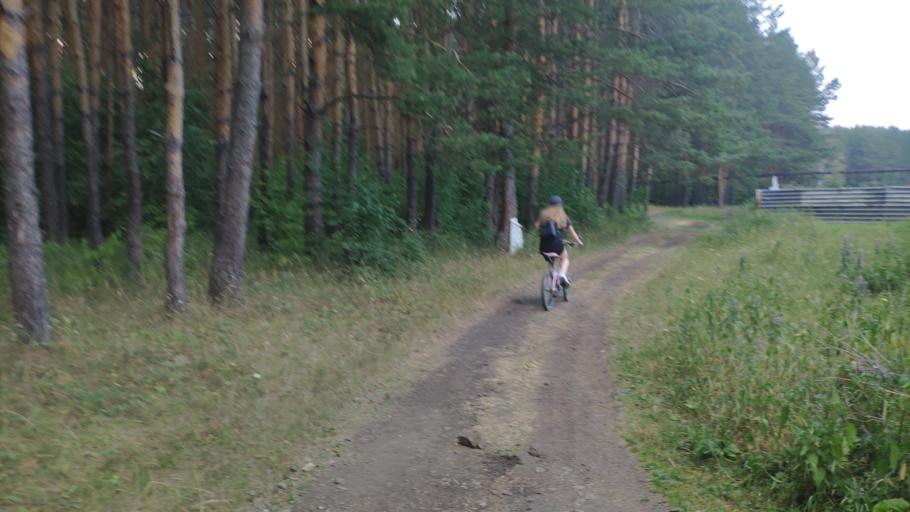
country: RU
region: Bashkortostan
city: Abzakovo
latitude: 53.8069
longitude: 58.6423
